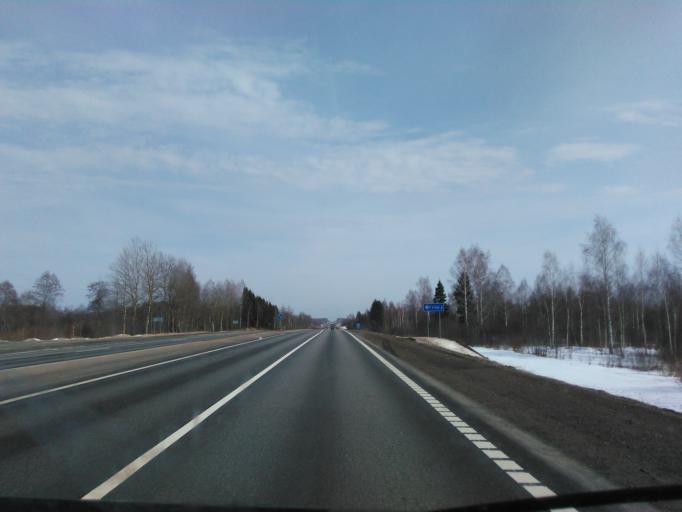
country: BY
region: Vitebsk
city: Dubrowna
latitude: 54.6897
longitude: 30.9192
